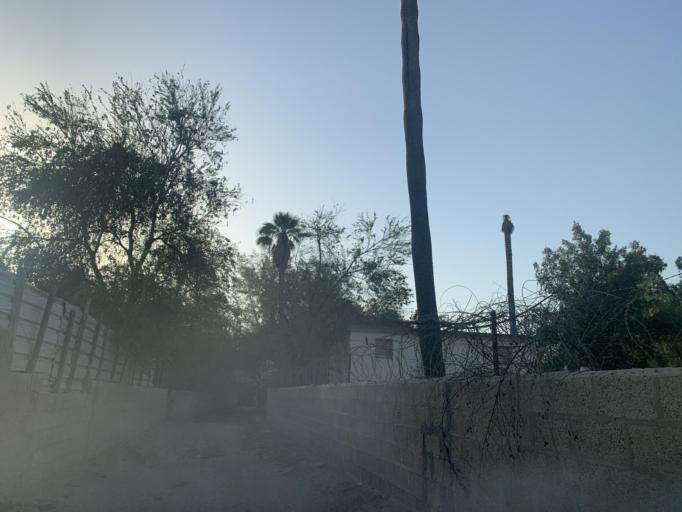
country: BH
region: Manama
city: Jidd Hafs
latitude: 26.2205
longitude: 50.5292
